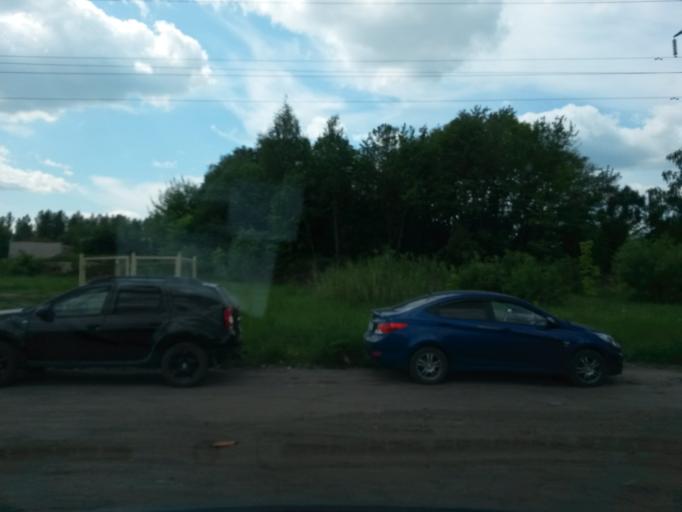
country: RU
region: Jaroslavl
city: Yaroslavl
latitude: 57.5775
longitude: 39.8864
